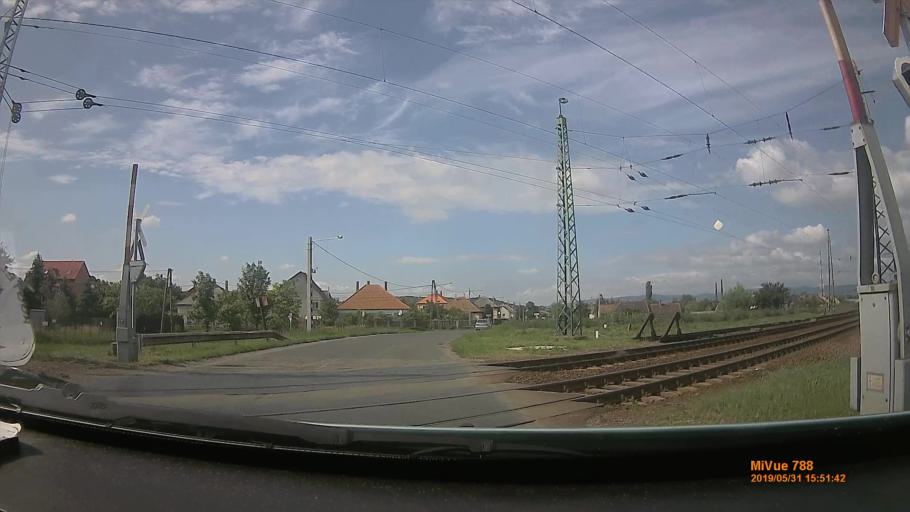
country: HU
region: Borsod-Abauj-Zemplen
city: Szerencs
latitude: 48.1464
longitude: 21.2007
